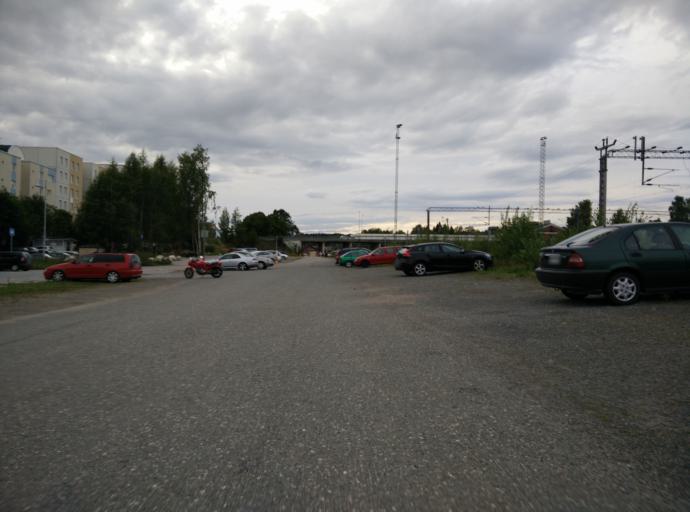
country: FI
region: Haeme
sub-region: Haemeenlinna
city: Haemeenlinna
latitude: 60.9990
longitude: 24.4841
